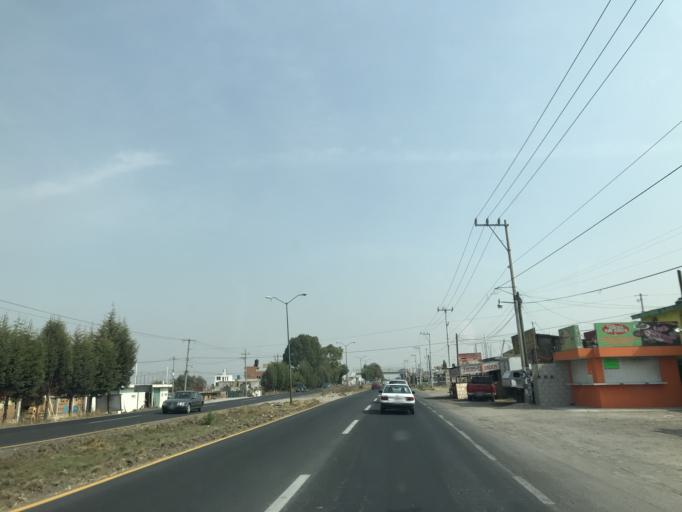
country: MX
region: Tlaxcala
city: Tenancingo
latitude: 19.1453
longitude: -98.1920
